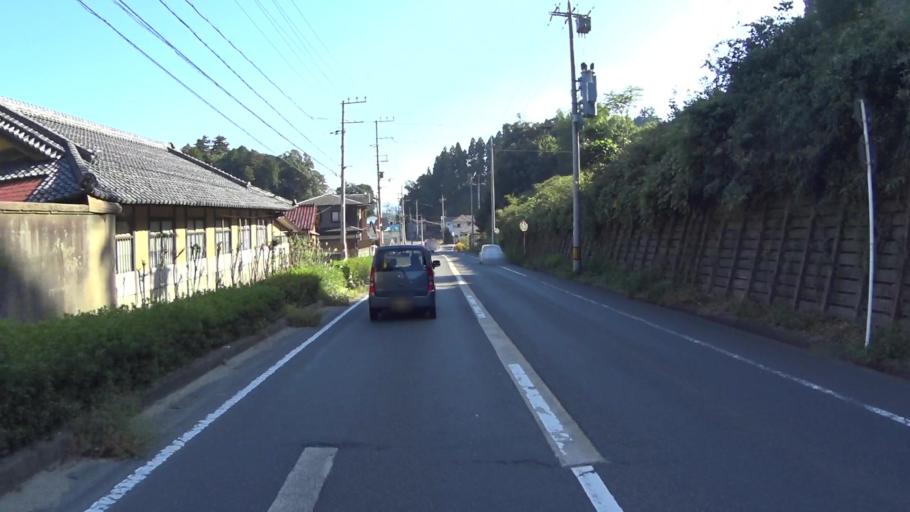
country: JP
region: Kyoto
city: Miyazu
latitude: 35.6329
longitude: 135.0543
